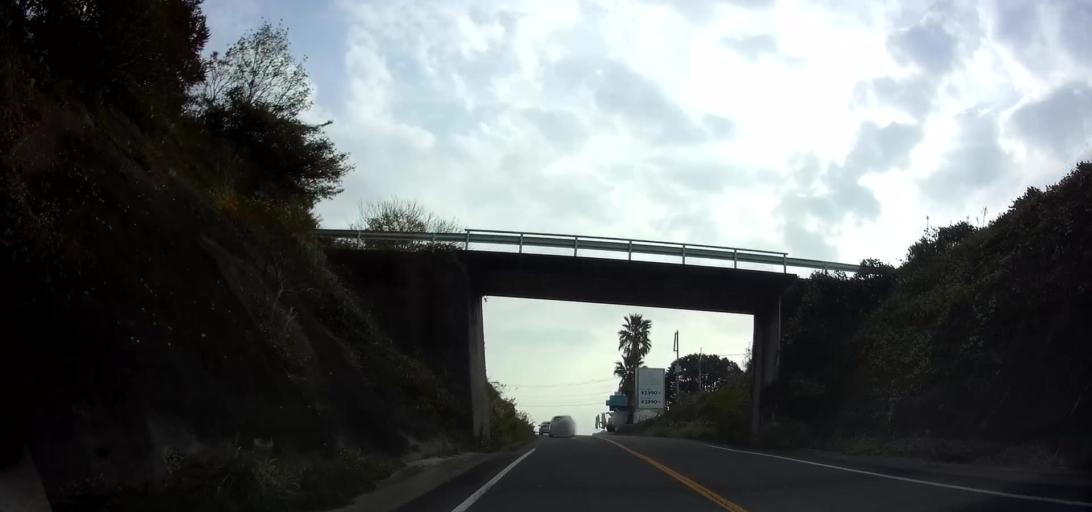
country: JP
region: Nagasaki
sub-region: Isahaya-shi
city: Isahaya
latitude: 32.7953
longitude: 130.0965
